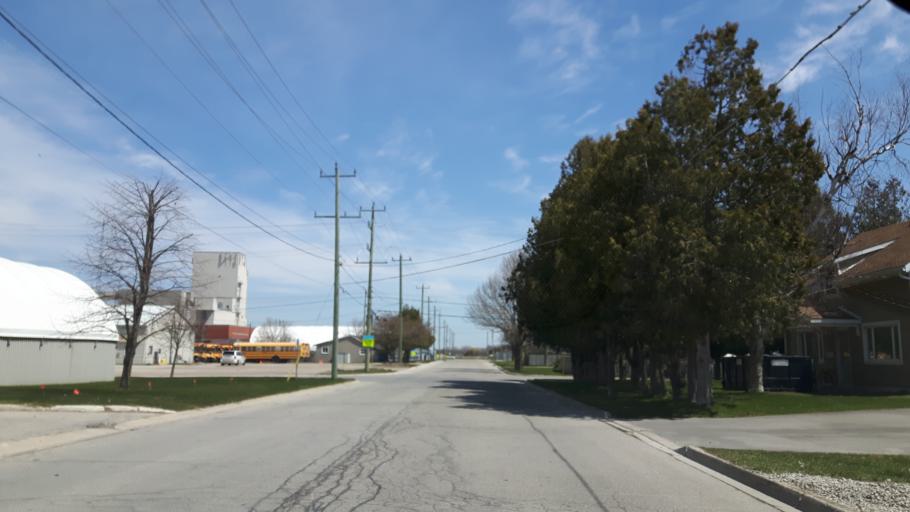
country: CA
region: Ontario
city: Goderich
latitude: 43.7364
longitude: -81.6979
